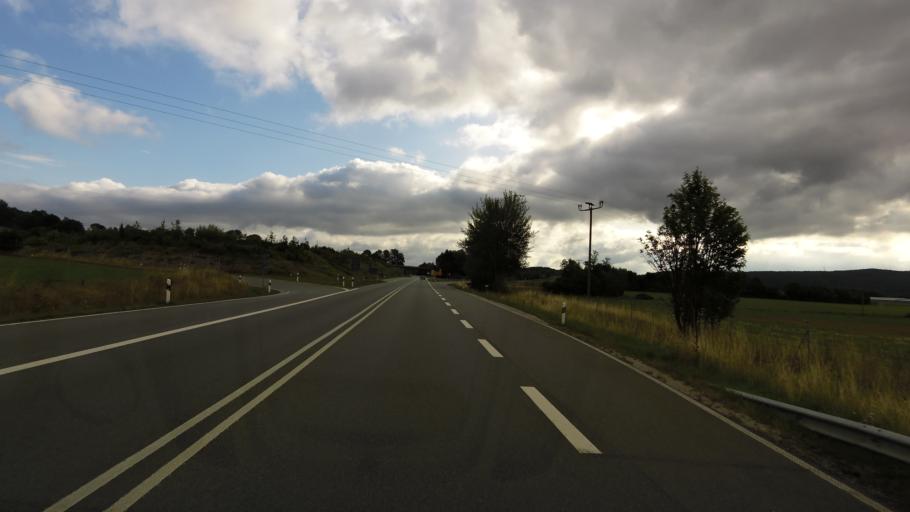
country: DE
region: Bavaria
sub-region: Upper Palatinate
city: Arnschwang
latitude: 49.2809
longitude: 12.7935
